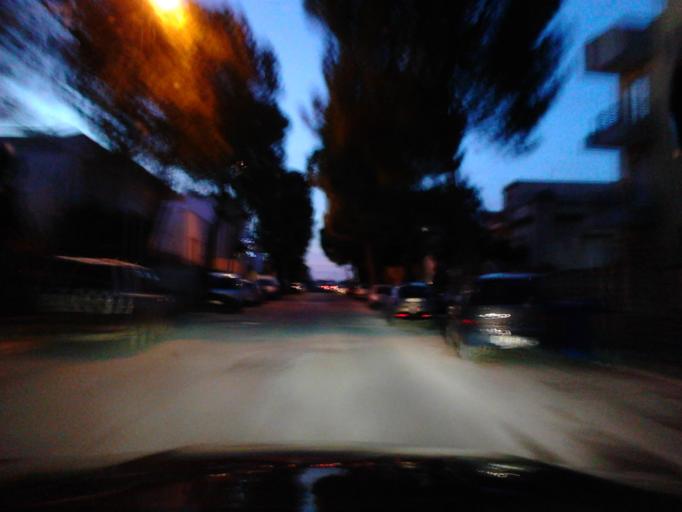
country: IT
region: Apulia
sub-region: Provincia di Bari
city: Adelfia
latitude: 41.0048
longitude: 16.8622
